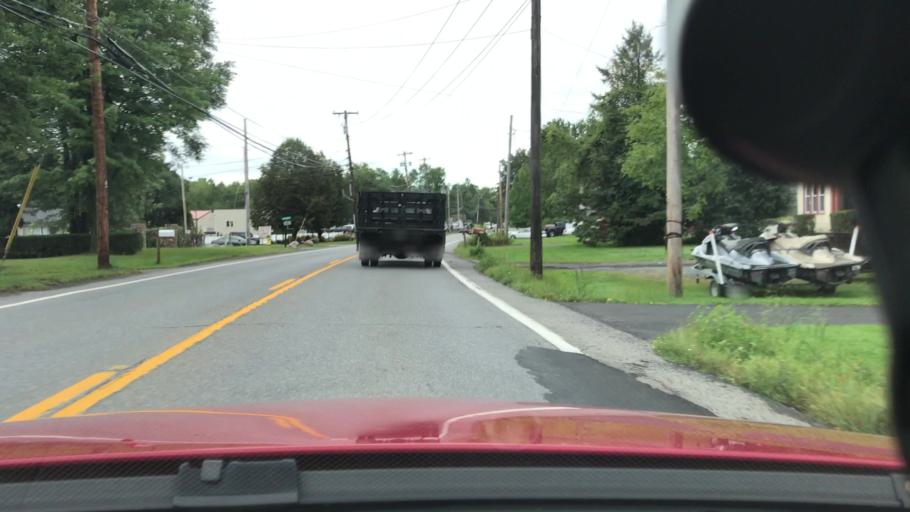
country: US
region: New York
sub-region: Saratoga County
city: Waterford
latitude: 42.8058
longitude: -73.6673
